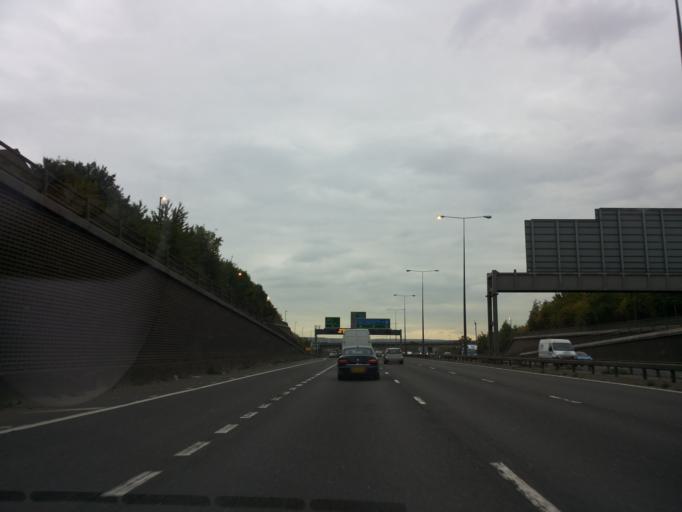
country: GB
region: England
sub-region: Kent
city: Dartford
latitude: 51.4368
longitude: 0.2391
